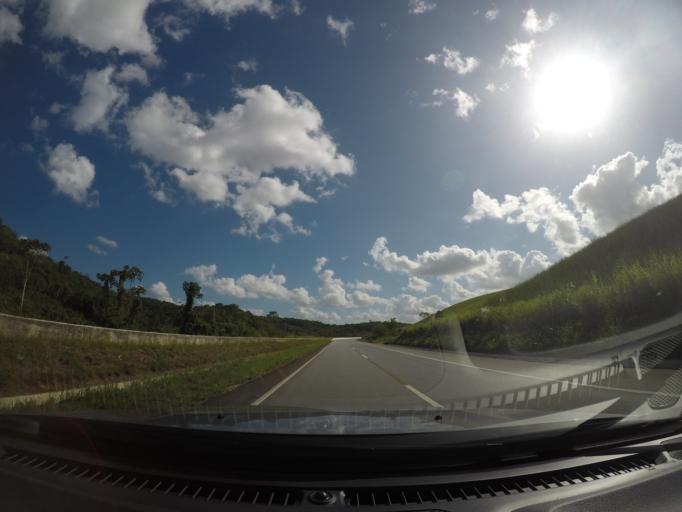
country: BR
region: Pernambuco
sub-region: Palmares
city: Palmares
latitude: -8.7669
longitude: -35.6159
